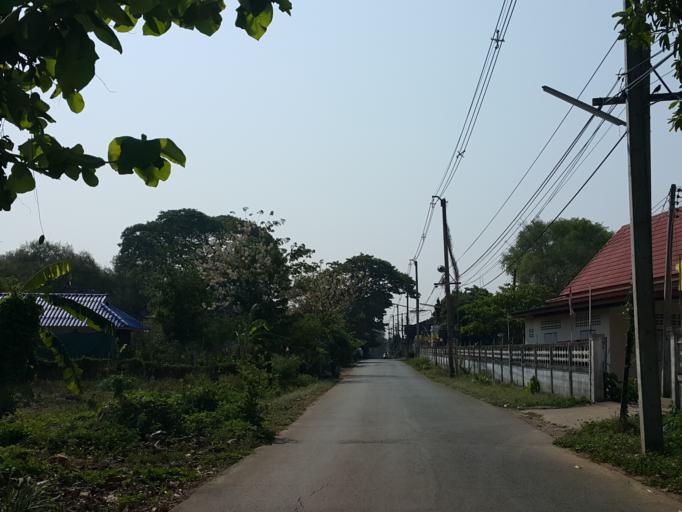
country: TH
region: Kanchanaburi
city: Sai Yok
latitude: 14.1207
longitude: 99.1366
